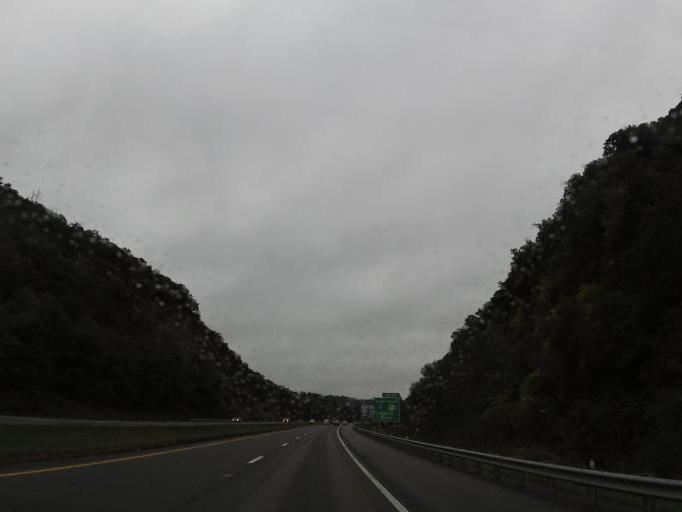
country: US
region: Virginia
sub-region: Wythe County
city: Wytheville
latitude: 36.9937
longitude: -81.0796
